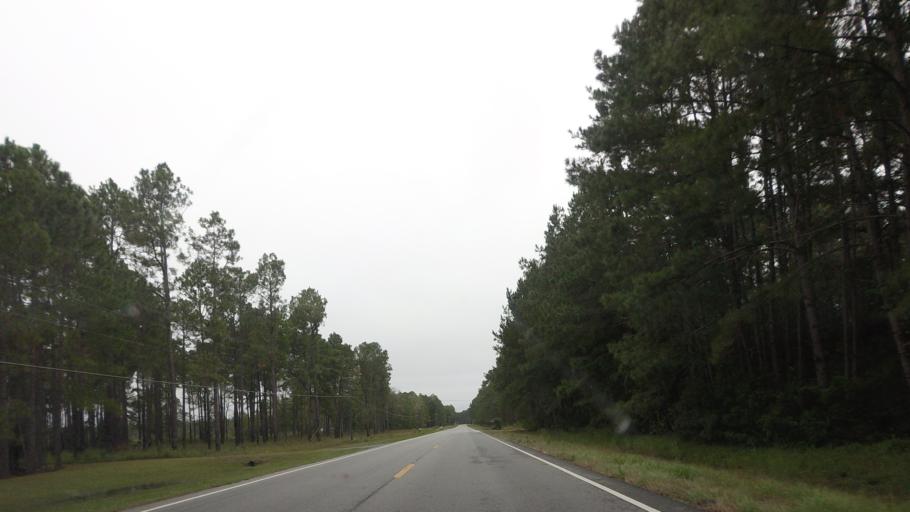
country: US
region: Georgia
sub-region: Berrien County
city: Nashville
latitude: 31.2466
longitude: -83.2426
